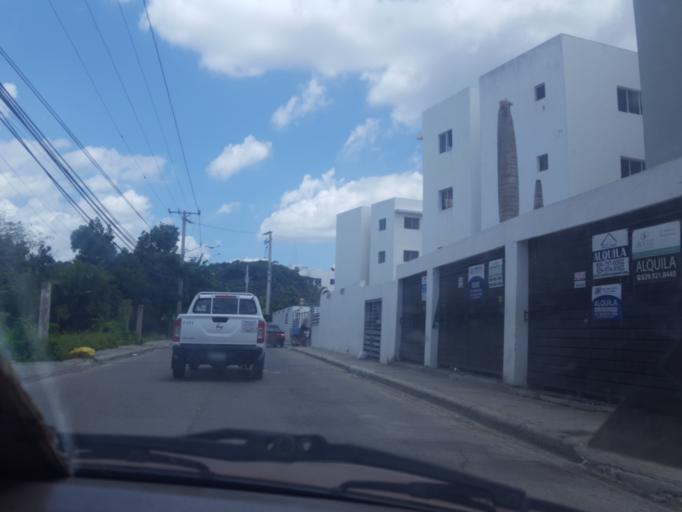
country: DO
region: Santiago
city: Santiago de los Caballeros
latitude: 19.4723
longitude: -70.6659
